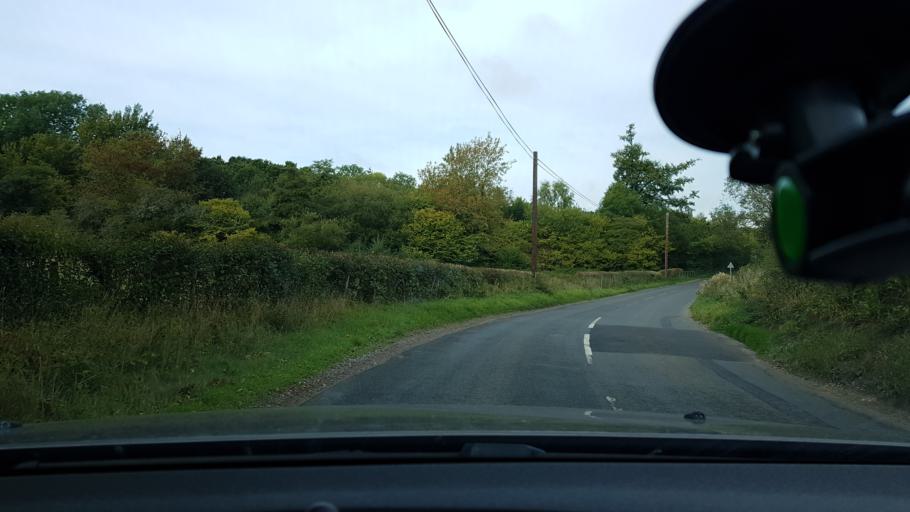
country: GB
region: England
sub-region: West Berkshire
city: Kintbury
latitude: 51.3875
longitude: -1.4281
